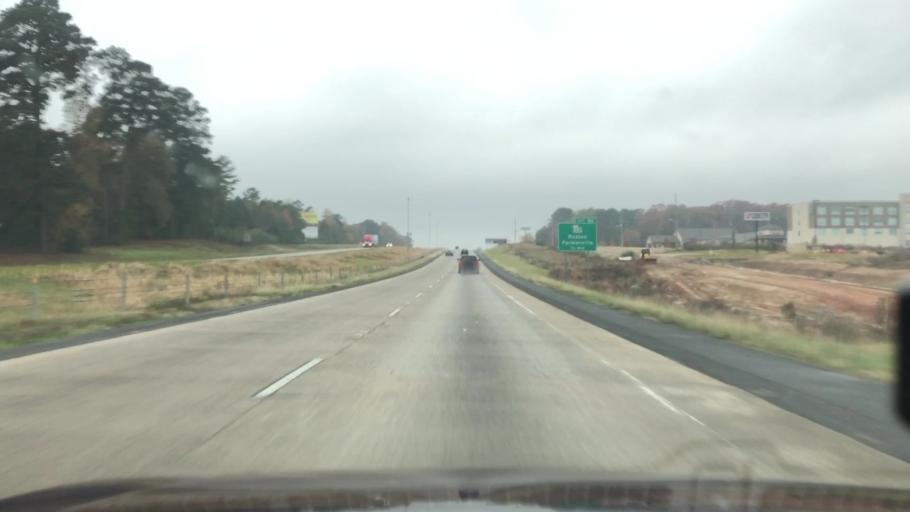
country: US
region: Louisiana
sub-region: Lincoln Parish
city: Ruston
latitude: 32.5405
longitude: -92.6041
